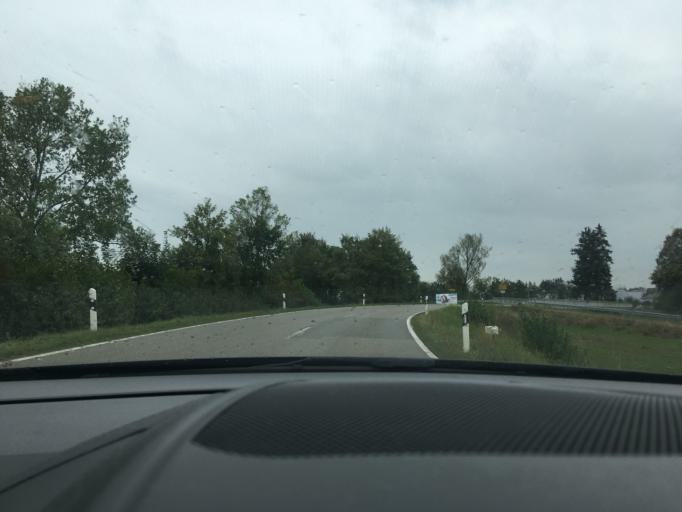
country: DE
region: Bavaria
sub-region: Swabia
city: Heimertingen
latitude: 48.0399
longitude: 10.1201
